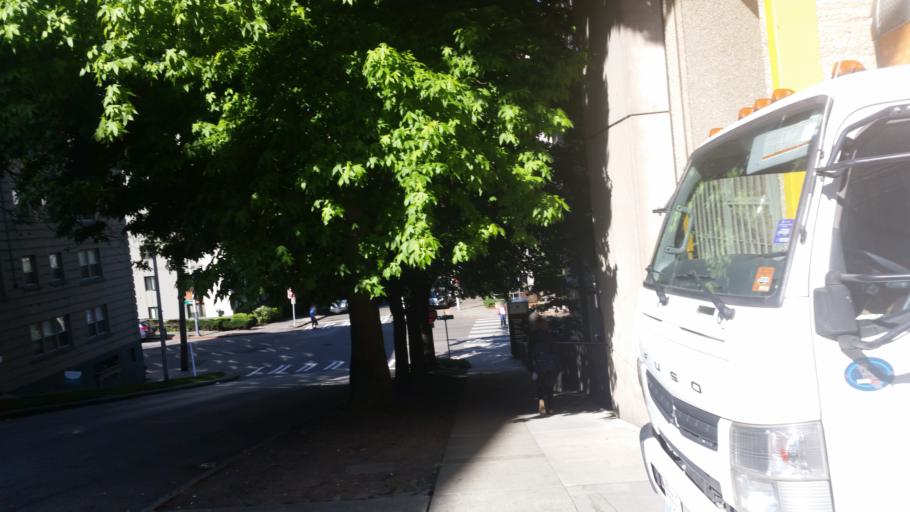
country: US
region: Washington
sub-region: King County
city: Seattle
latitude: 47.6094
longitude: -122.3274
